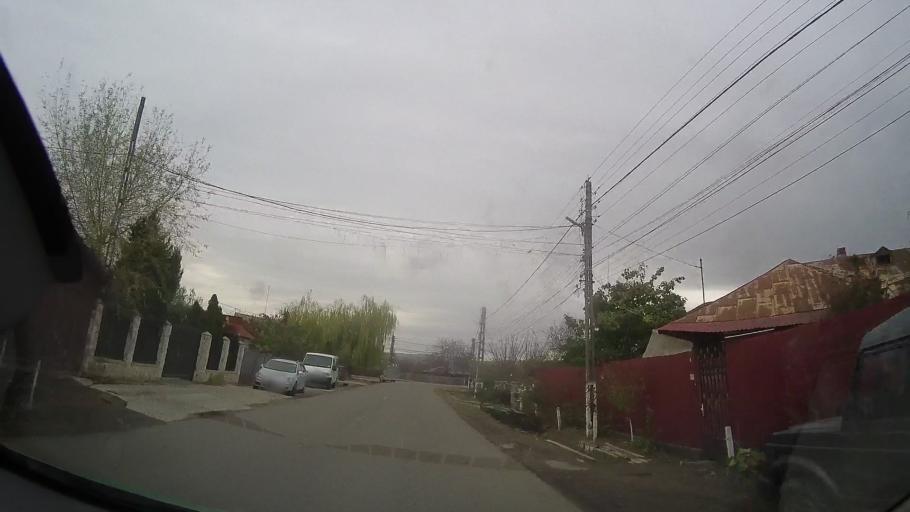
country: RO
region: Prahova
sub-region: Comuna Vadu Sapat
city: Vadu Sapat
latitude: 45.0308
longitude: 26.3846
